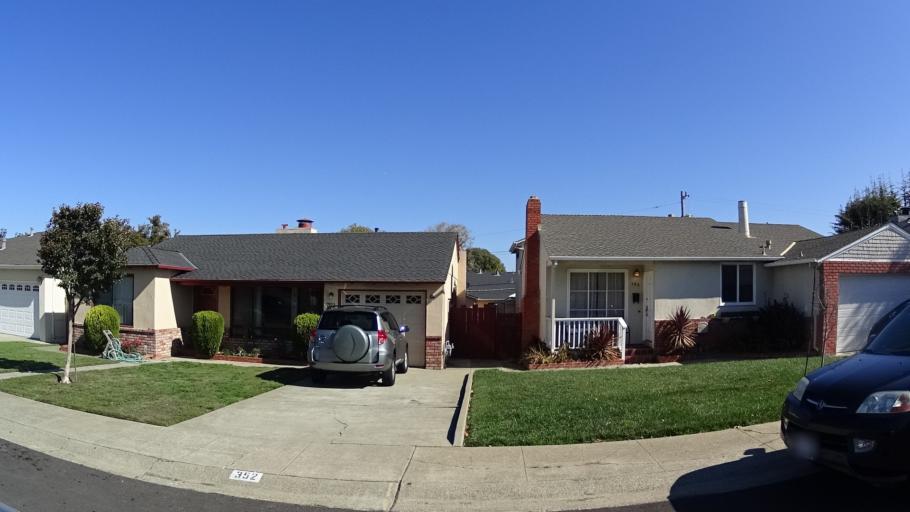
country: US
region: California
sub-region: San Mateo County
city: San Bruno
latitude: 37.6248
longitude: -122.4229
